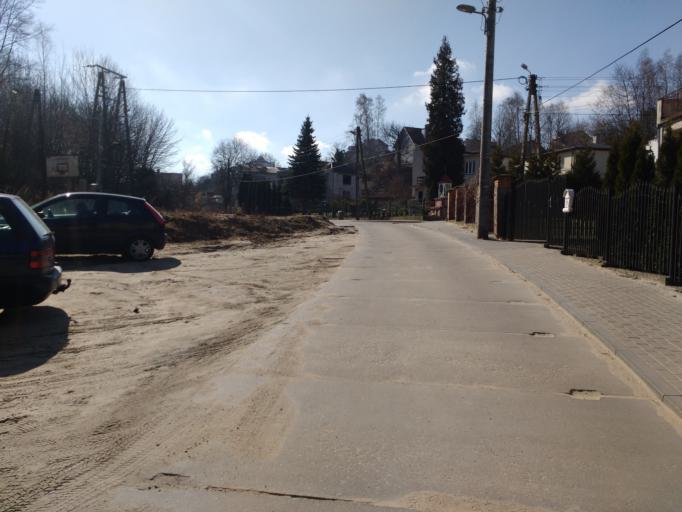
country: PL
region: Pomeranian Voivodeship
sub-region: Gdynia
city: Wielki Kack
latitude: 54.4768
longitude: 18.5116
